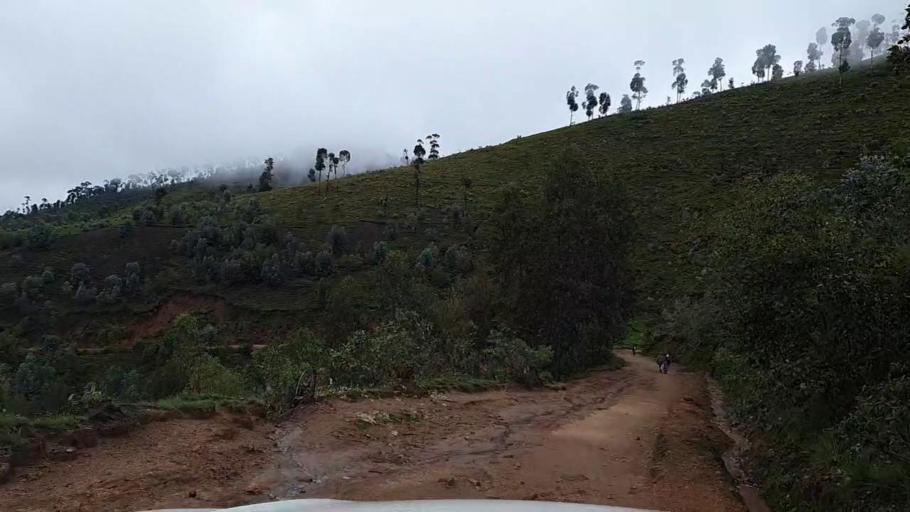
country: RW
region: Southern Province
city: Nzega
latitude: -2.3972
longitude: 29.4995
